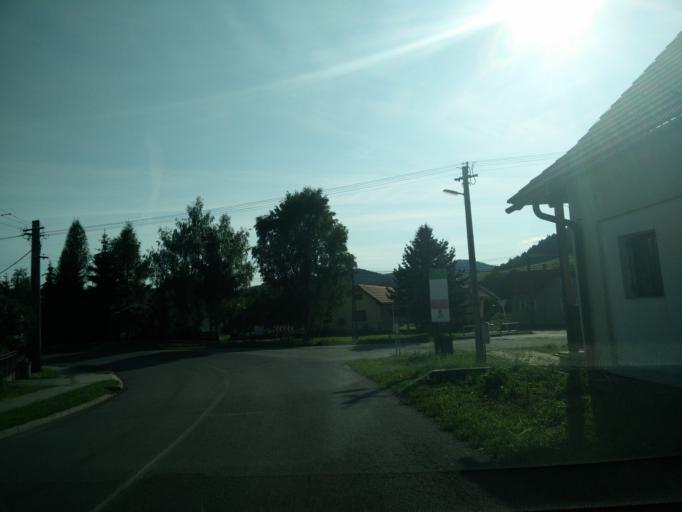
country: SK
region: Nitriansky
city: Handlova
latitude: 48.8851
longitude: 18.7473
